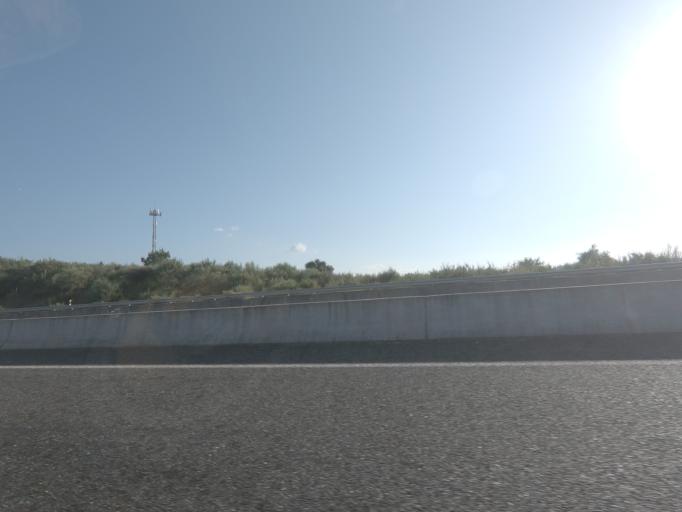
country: ES
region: Galicia
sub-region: Provincia de Ourense
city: Oimbra
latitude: 41.8186
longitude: -7.4172
